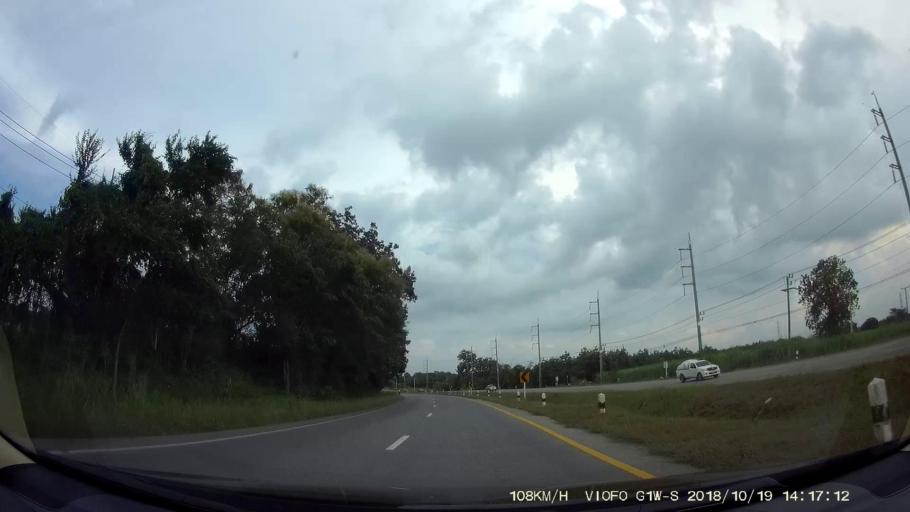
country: TH
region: Chaiyaphum
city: Khon Sawan
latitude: 16.0003
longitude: 102.2224
